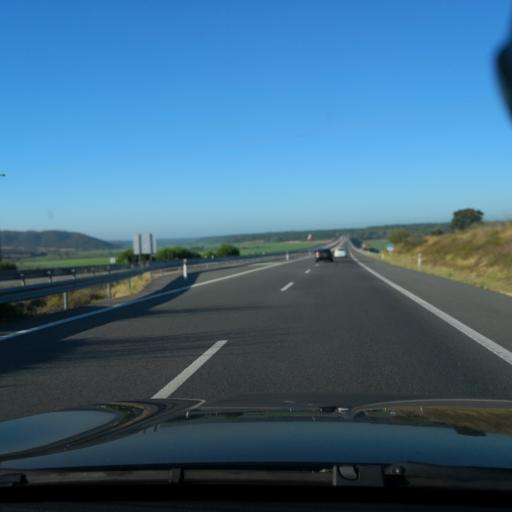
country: PT
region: Setubal
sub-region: Alcacer do Sal
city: Alcacer do Sal
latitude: 38.3697
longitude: -8.4884
